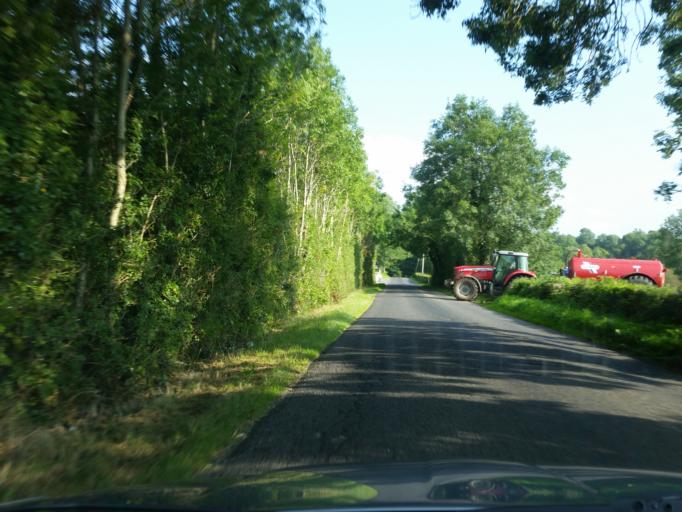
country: GB
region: Northern Ireland
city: Lisnaskea
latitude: 54.2864
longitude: -7.4414
